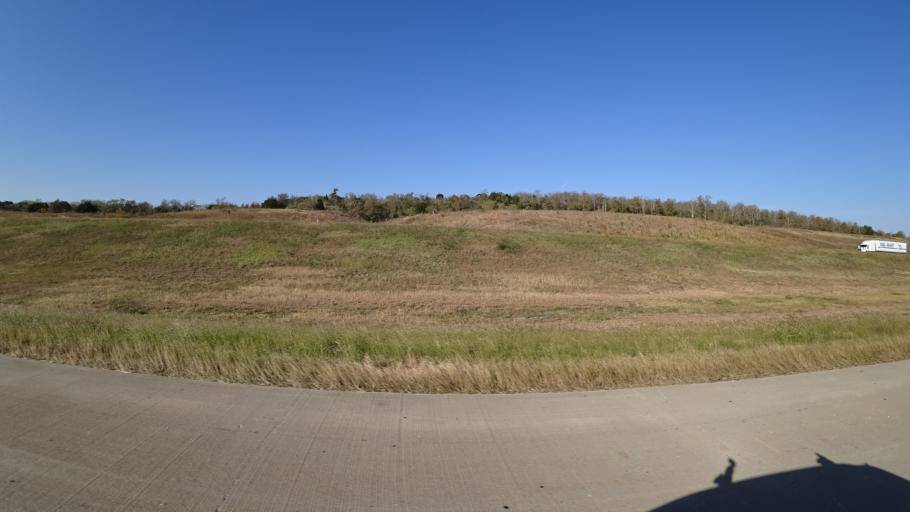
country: US
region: Texas
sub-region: Travis County
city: Manor
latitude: 30.3016
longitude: -97.5696
